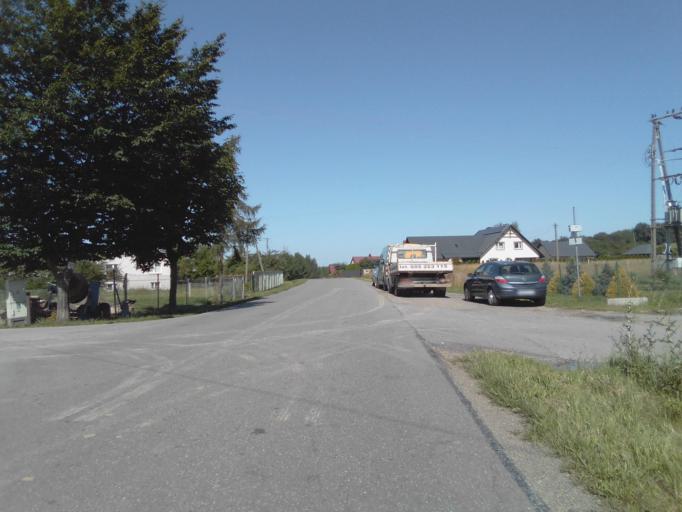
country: PL
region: Subcarpathian Voivodeship
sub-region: Powiat krosnienski
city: Dukla
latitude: 49.6018
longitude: 21.6856
